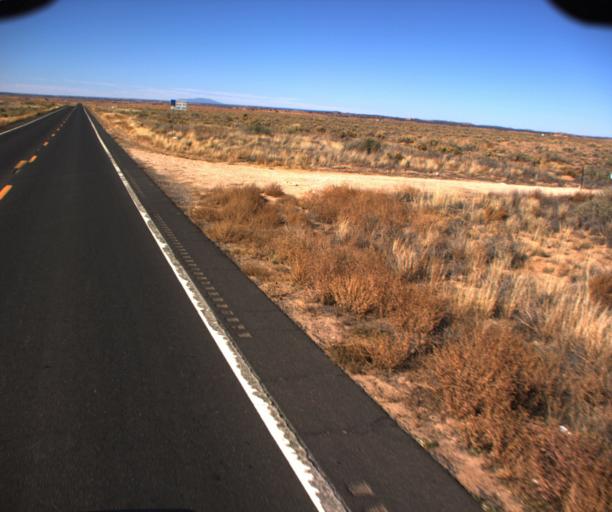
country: US
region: Arizona
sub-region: Coconino County
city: Kaibito
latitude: 36.4681
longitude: -110.6960
